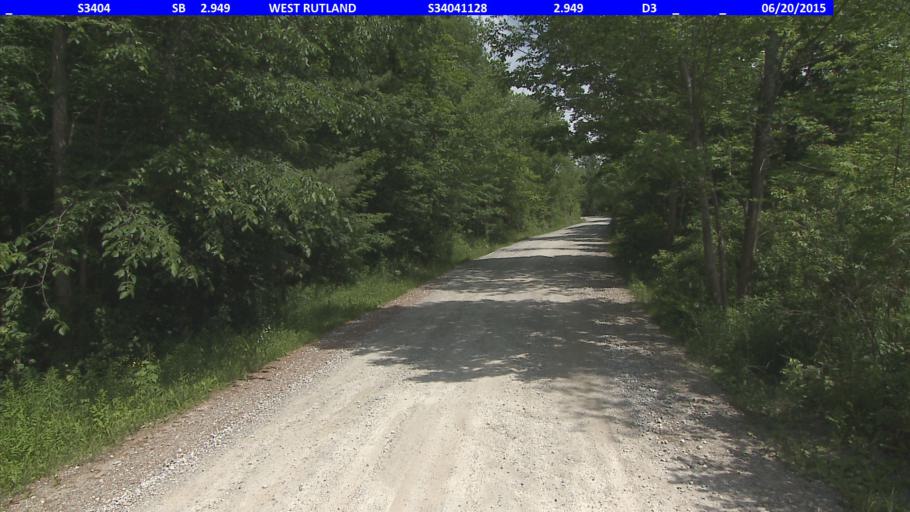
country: US
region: Vermont
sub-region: Rutland County
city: West Rutland
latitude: 43.6318
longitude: -73.0583
